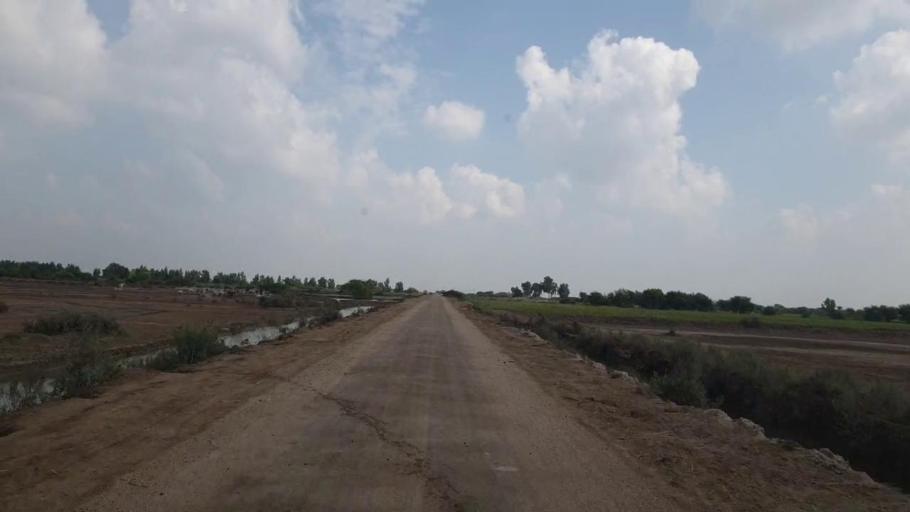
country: PK
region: Sindh
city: Badin
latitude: 24.5328
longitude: 68.6110
